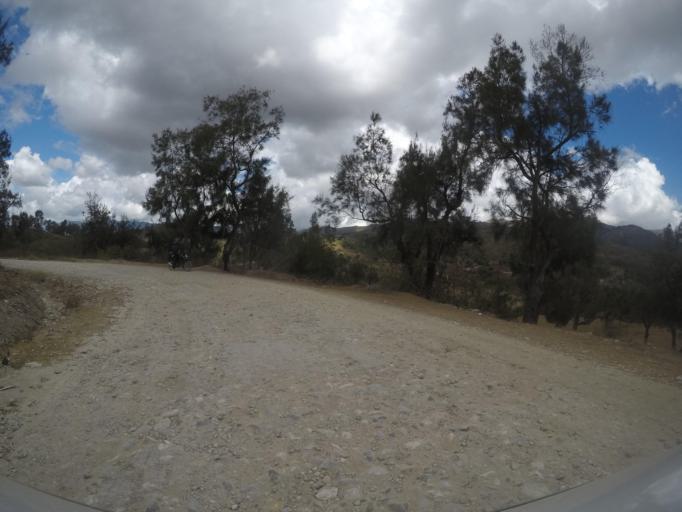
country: TL
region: Baucau
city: Baucau
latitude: -8.5009
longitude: 126.6776
